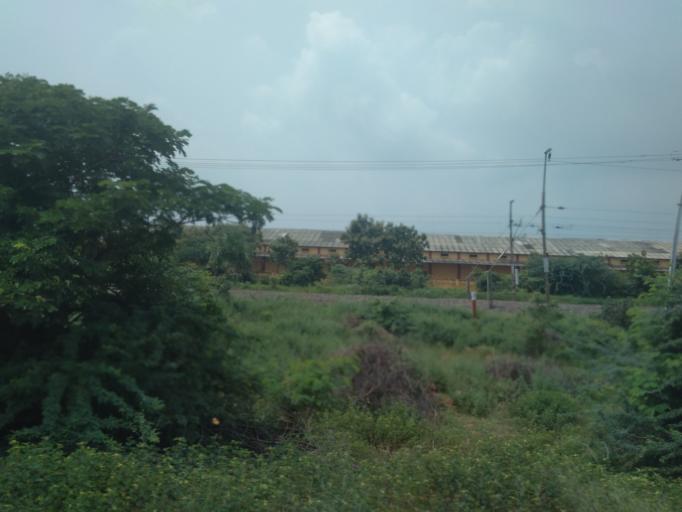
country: IN
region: Telangana
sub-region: Nalgonda
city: Bhongir
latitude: 17.5855
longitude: 78.9891
